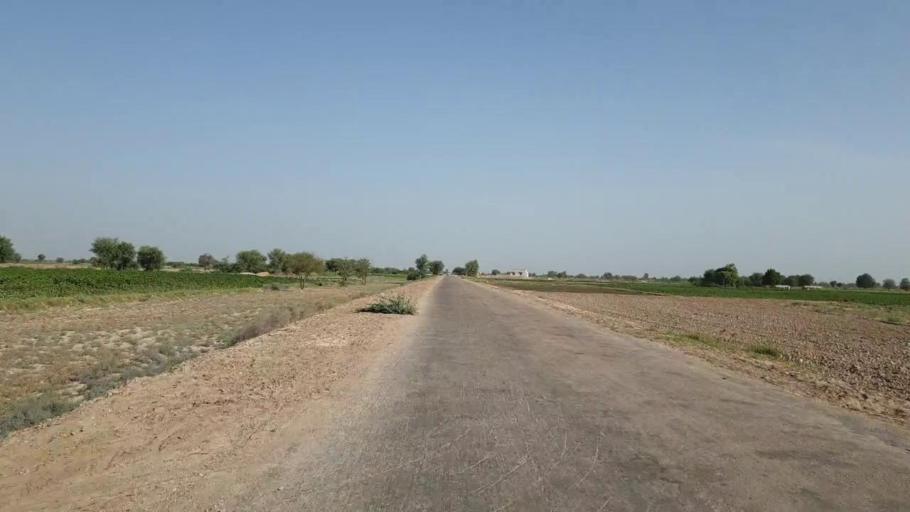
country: PK
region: Sindh
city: Nawabshah
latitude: 26.1448
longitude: 68.4503
